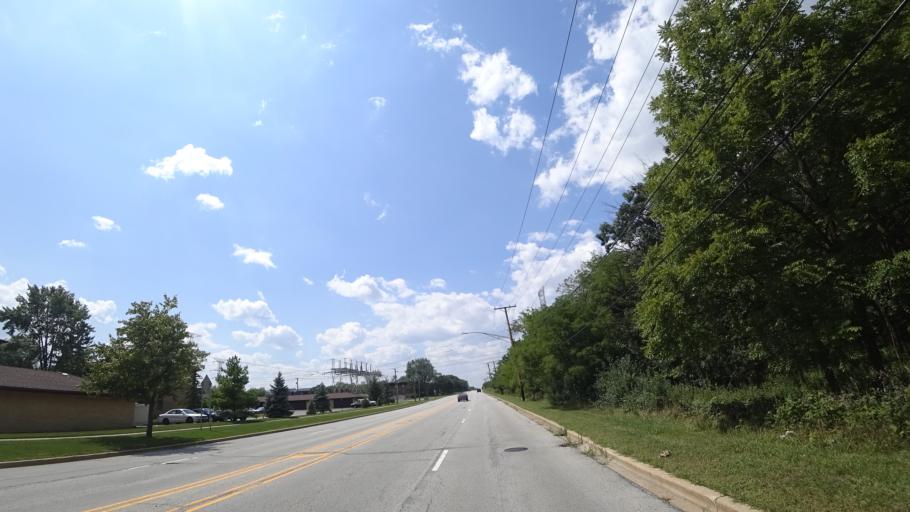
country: US
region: Illinois
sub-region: Cook County
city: Tinley Park
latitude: 41.6170
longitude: -87.7972
